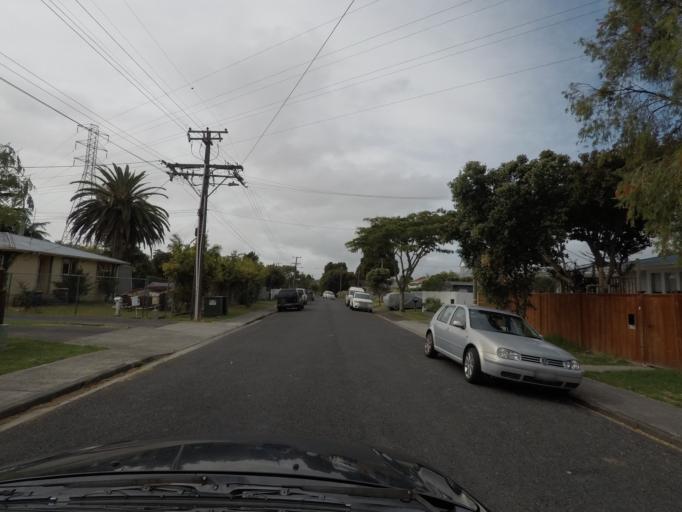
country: NZ
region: Auckland
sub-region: Auckland
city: Rosebank
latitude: -36.8922
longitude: 174.6664
